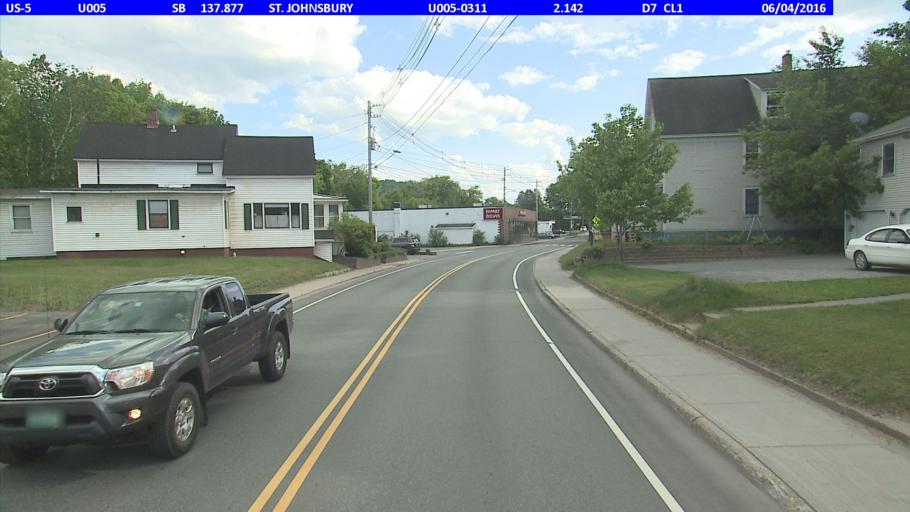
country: US
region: Vermont
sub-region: Caledonia County
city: St Johnsbury
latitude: 44.4239
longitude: -72.0147
